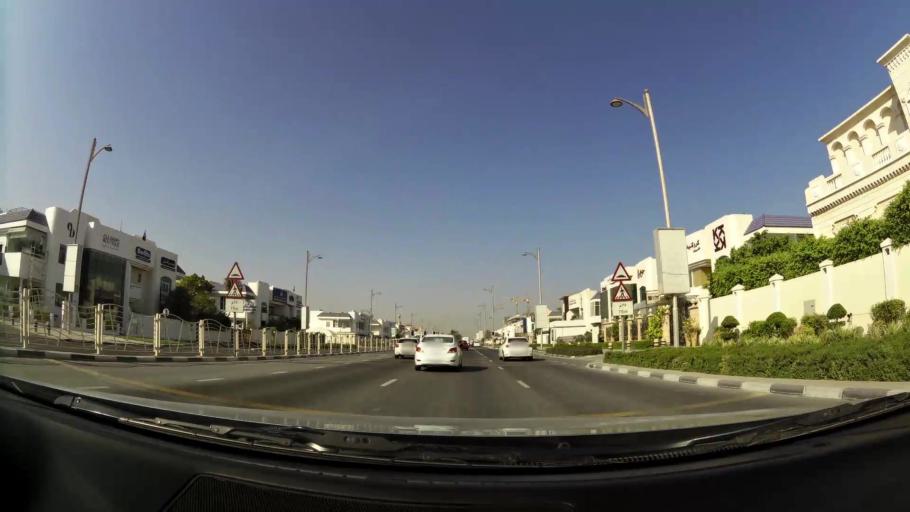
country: AE
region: Dubai
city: Dubai
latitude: 25.2208
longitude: 55.2548
